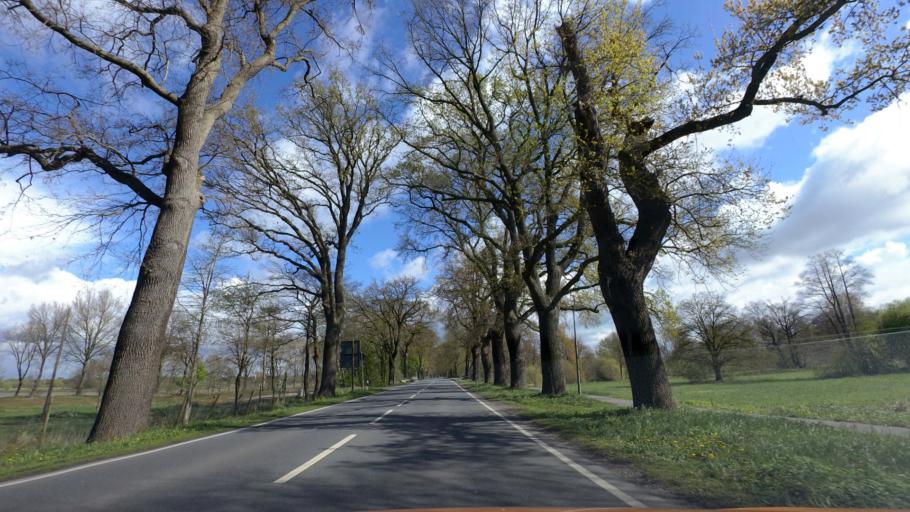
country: DE
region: Lower Saxony
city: Ottersberg
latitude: 53.1006
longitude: 9.1285
